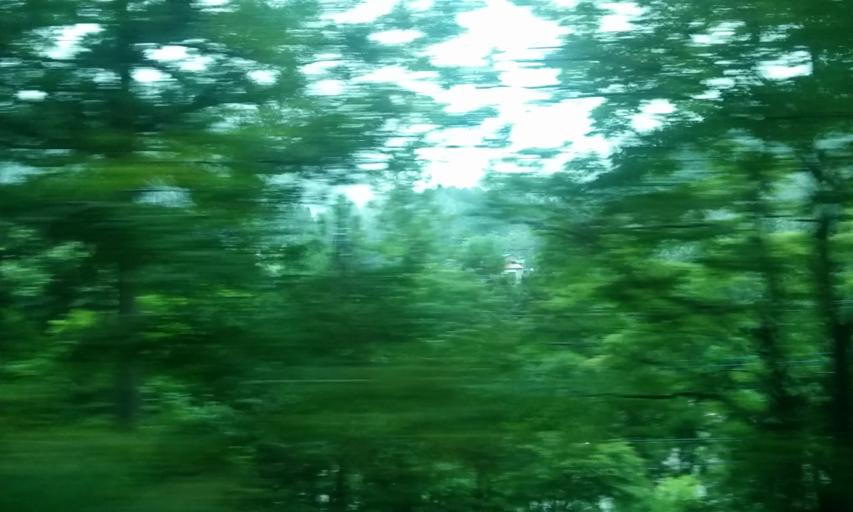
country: JP
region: Tokyo
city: Ome
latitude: 35.8047
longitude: 139.1774
